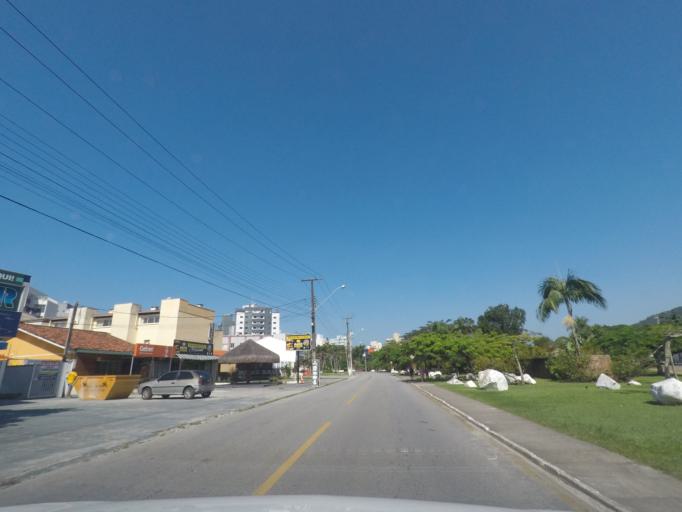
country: BR
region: Parana
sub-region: Guaratuba
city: Guaratuba
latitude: -25.8326
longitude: -48.5398
